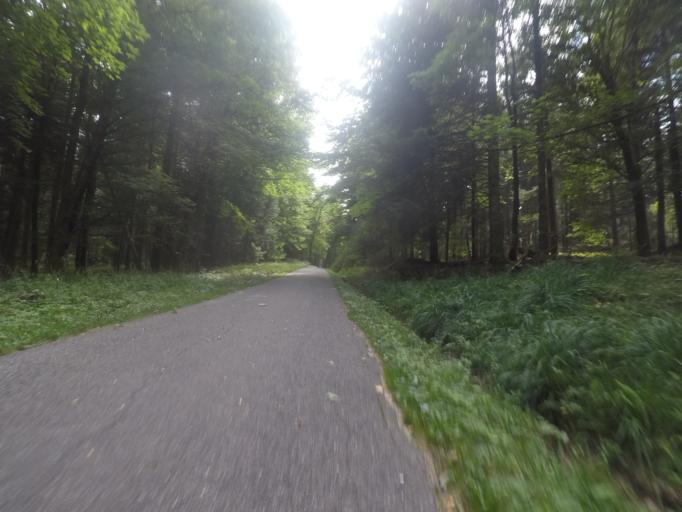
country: DE
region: Baden-Wuerttemberg
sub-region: Karlsruhe Region
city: Dobel
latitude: 48.7843
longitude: 8.4699
